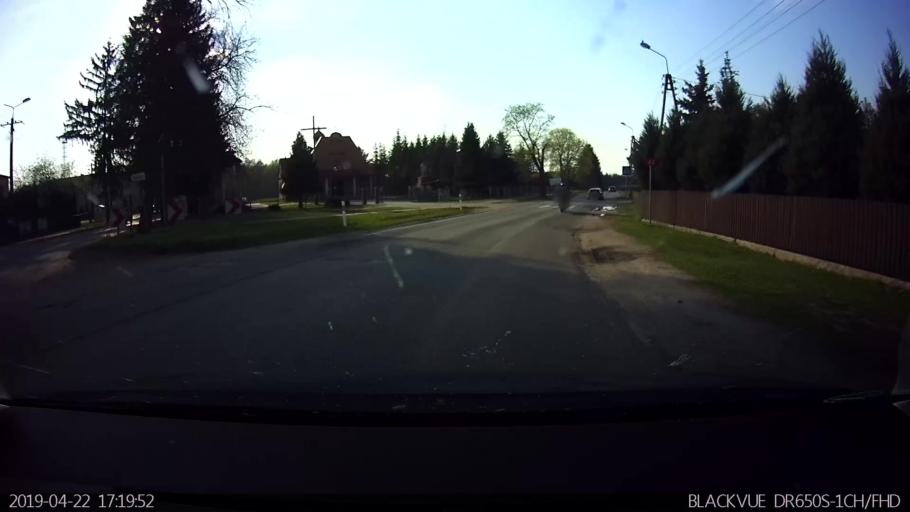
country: PL
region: Masovian Voivodeship
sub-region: Powiat sokolowski
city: Repki
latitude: 52.3853
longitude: 22.3884
